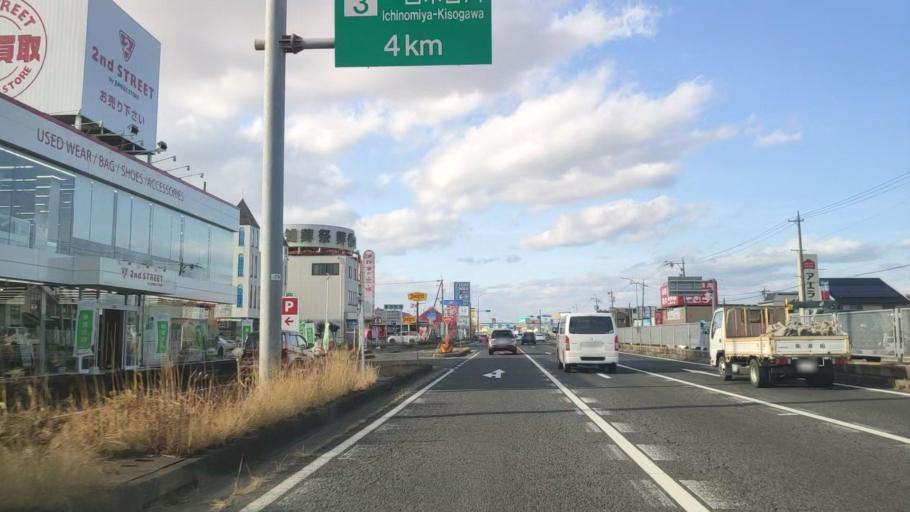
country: JP
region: Aichi
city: Ichinomiya
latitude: 35.3074
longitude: 136.8199
